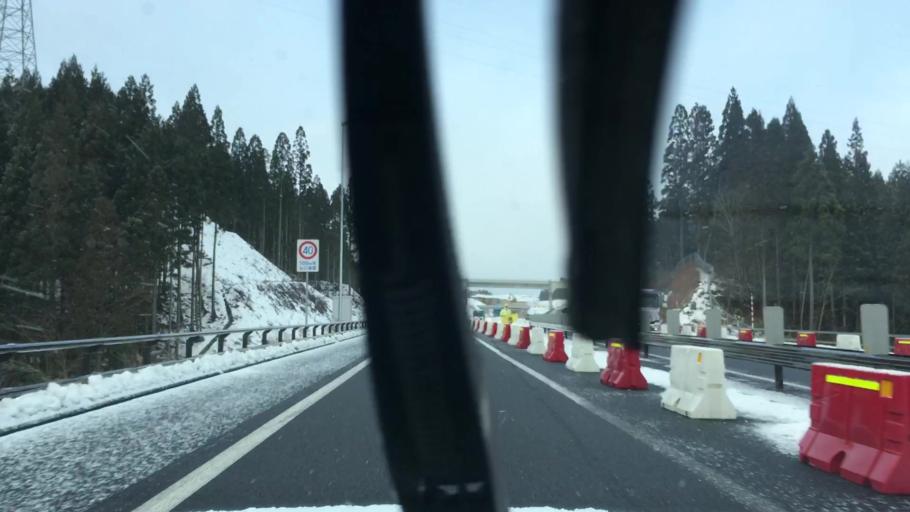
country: JP
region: Akita
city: Takanosu
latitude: 40.1987
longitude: 140.3802
